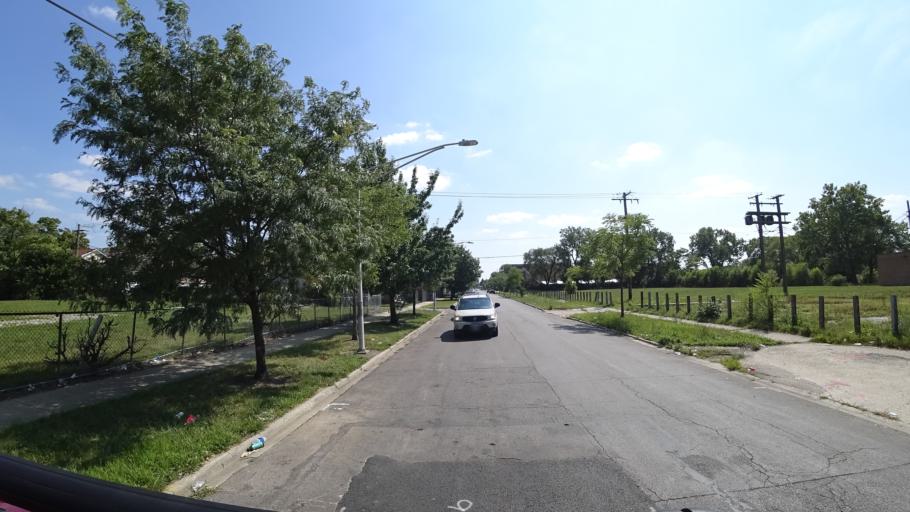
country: US
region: Illinois
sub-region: Cook County
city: Cicero
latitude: 41.8587
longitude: -87.7298
